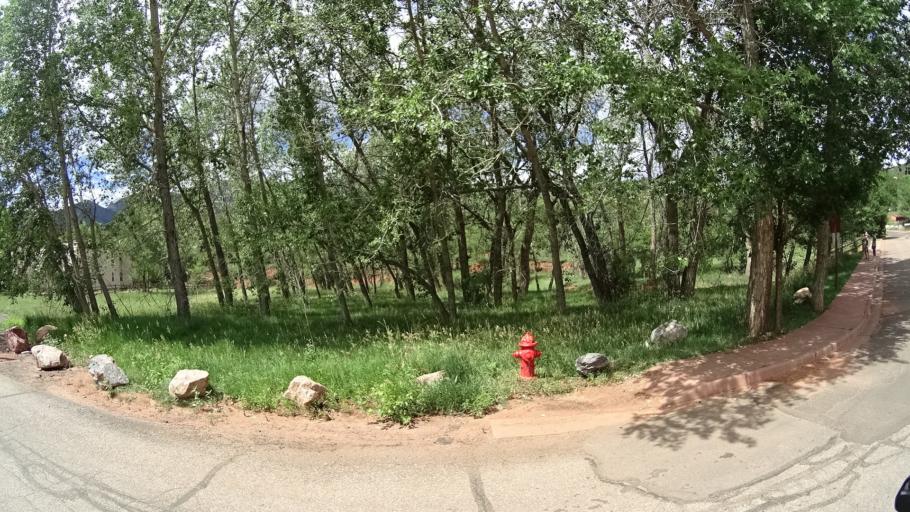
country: US
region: Colorado
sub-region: El Paso County
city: Manitou Springs
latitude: 38.8630
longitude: -104.8927
